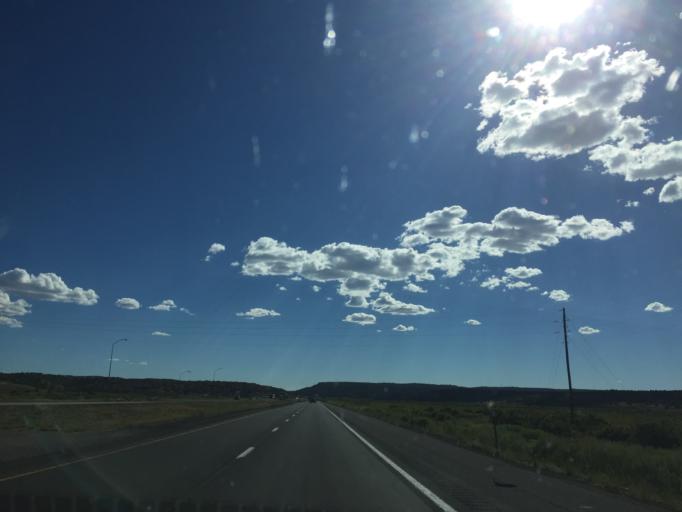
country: US
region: New Mexico
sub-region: McKinley County
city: Gallup
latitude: 35.4835
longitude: -108.9084
